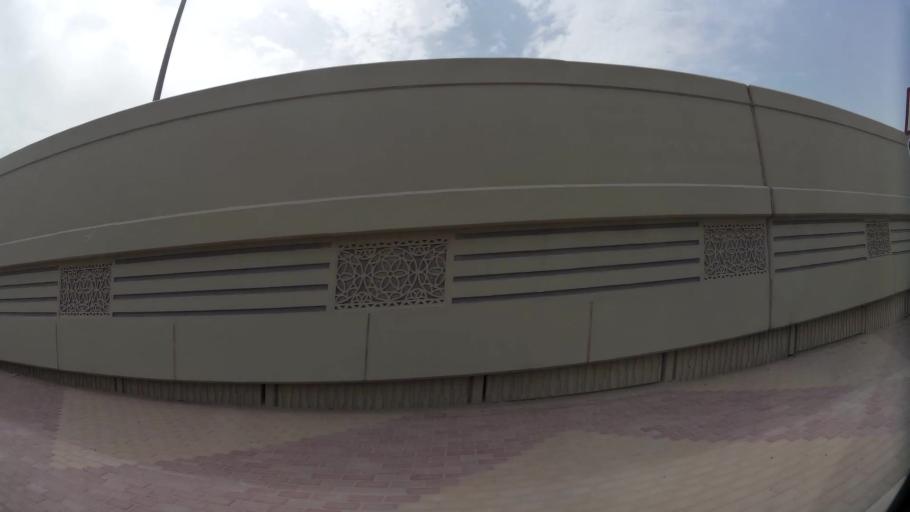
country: QA
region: Baladiyat ad Dawhah
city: Doha
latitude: 25.2952
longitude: 51.4777
